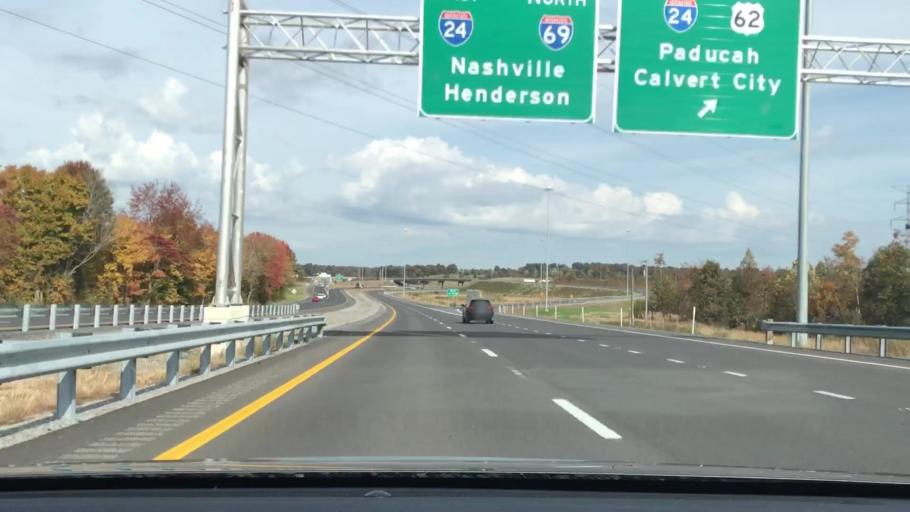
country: US
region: Kentucky
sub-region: Marshall County
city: Calvert City
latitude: 36.9795
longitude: -88.3456
